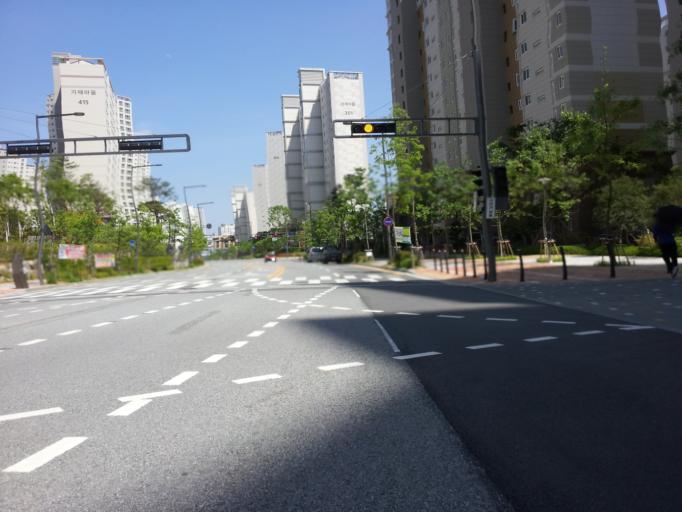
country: KR
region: Chungcheongnam-do
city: Gongju
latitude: 36.5054
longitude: 127.2396
